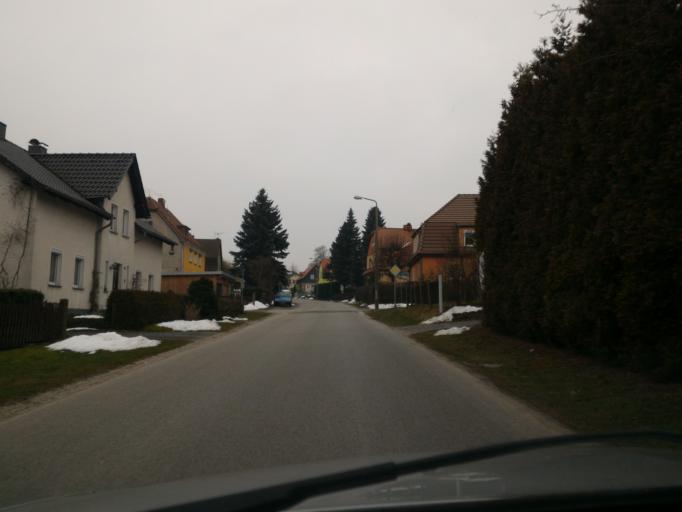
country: DE
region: Saxony
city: Neugersdorf
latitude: 50.9715
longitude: 14.6147
